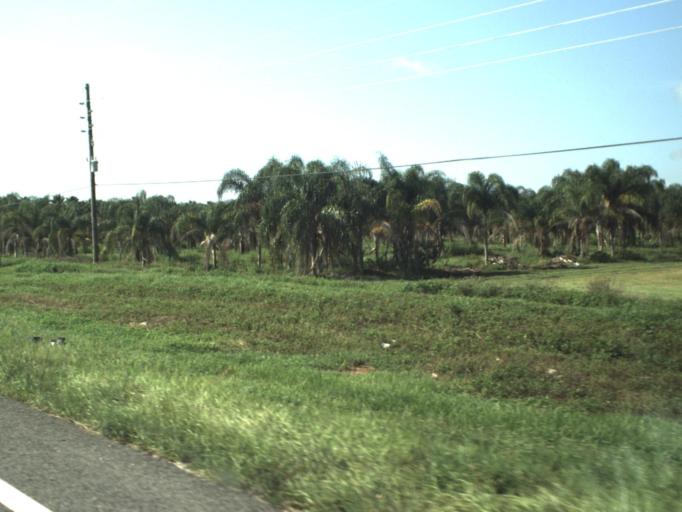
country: US
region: Florida
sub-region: Palm Beach County
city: Belle Glade Camp
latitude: 26.4926
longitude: -80.6602
